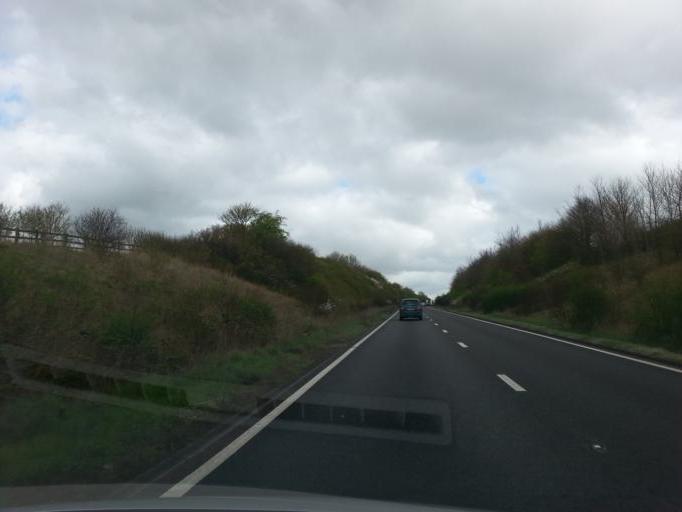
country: GB
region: England
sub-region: Wiltshire
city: Winterbourne Stoke
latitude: 51.1583
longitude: -1.9581
